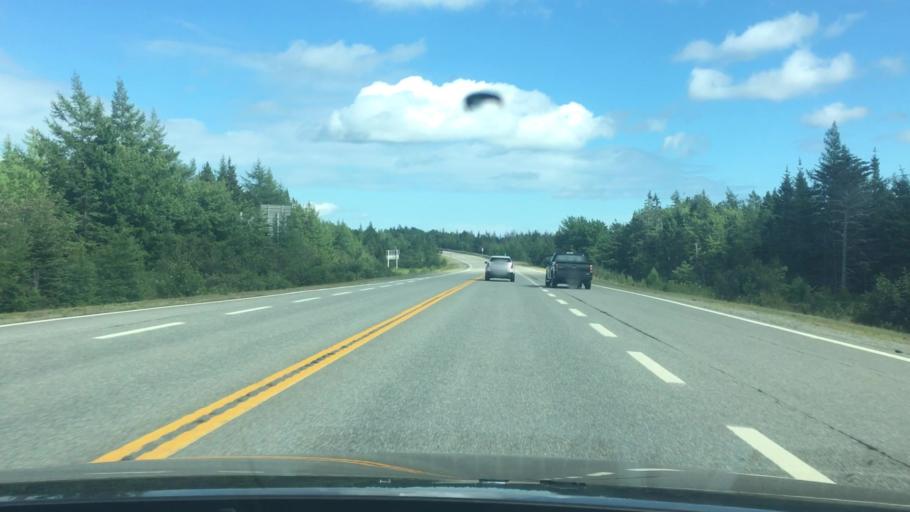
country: CA
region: Nova Scotia
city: Princeville
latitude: 45.6118
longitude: -61.0753
